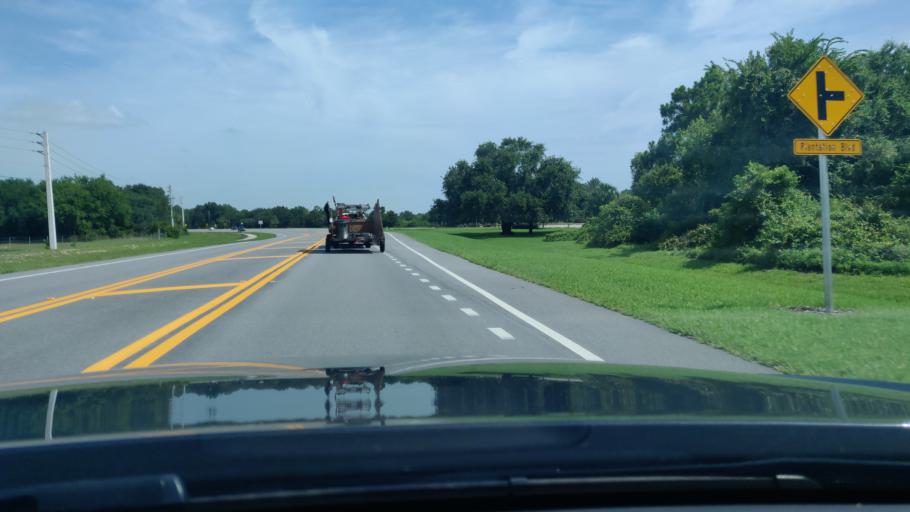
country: US
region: Florida
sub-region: Flagler County
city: Flagler Beach
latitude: 29.5151
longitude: -81.1637
